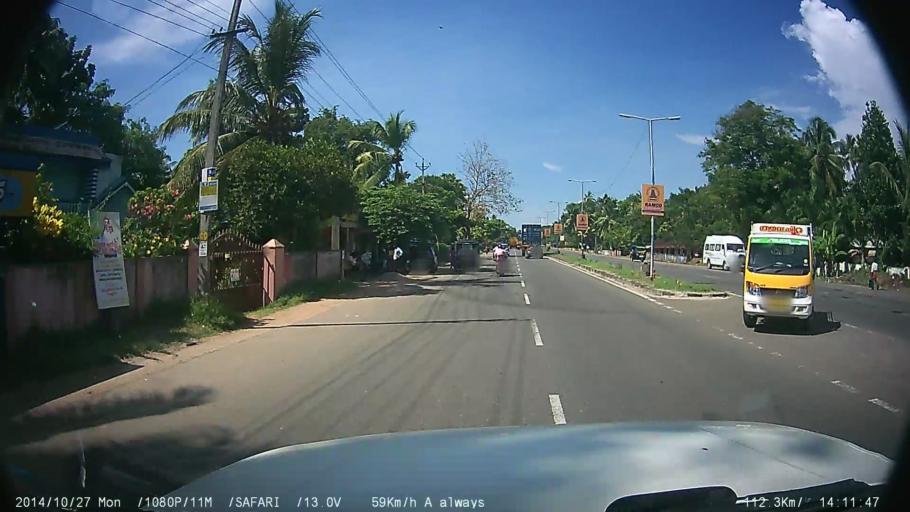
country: IN
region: Kerala
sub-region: Alappuzha
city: Kutiatodu
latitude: 9.7966
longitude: 76.3157
